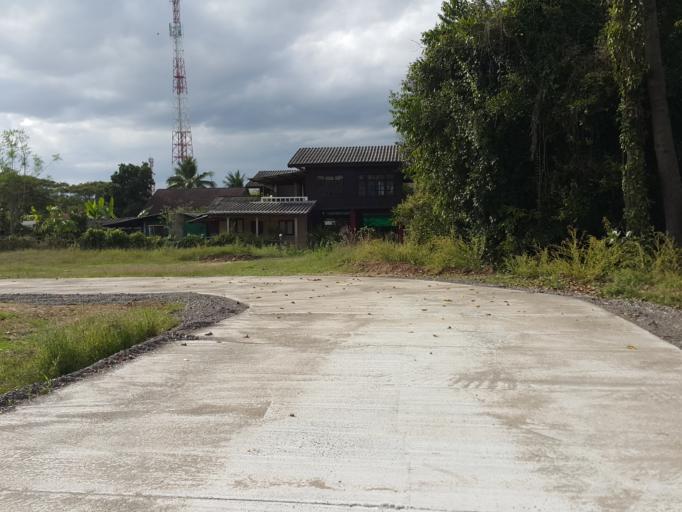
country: TH
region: Chiang Mai
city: San Sai
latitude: 18.8918
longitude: 99.0955
